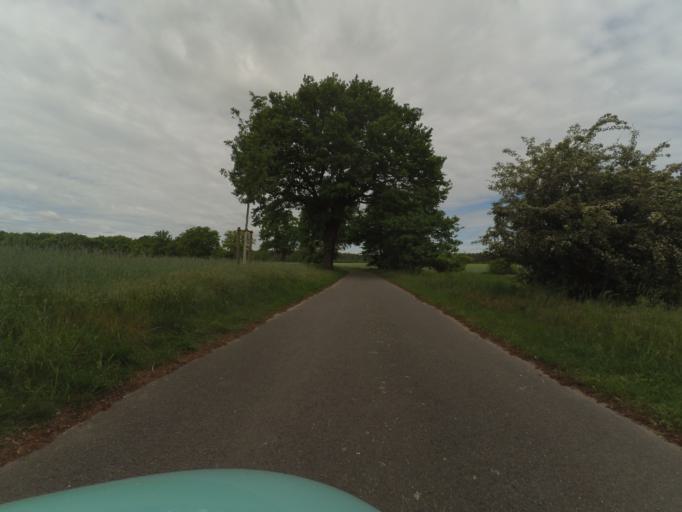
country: DE
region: Lower Saxony
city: Wunstorf
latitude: 52.4373
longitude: 9.4983
